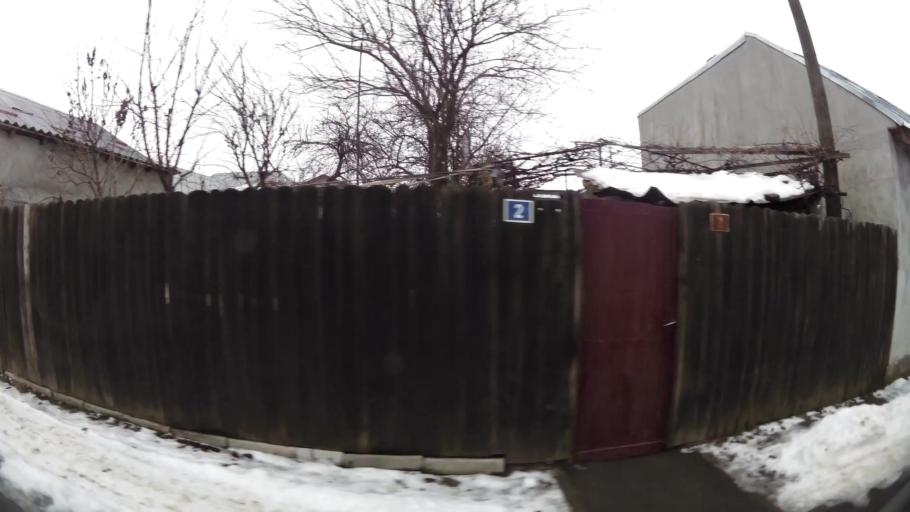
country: RO
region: Ilfov
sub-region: Comuna Pantelimon
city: Pantelimon
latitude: 44.4545
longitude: 26.1959
